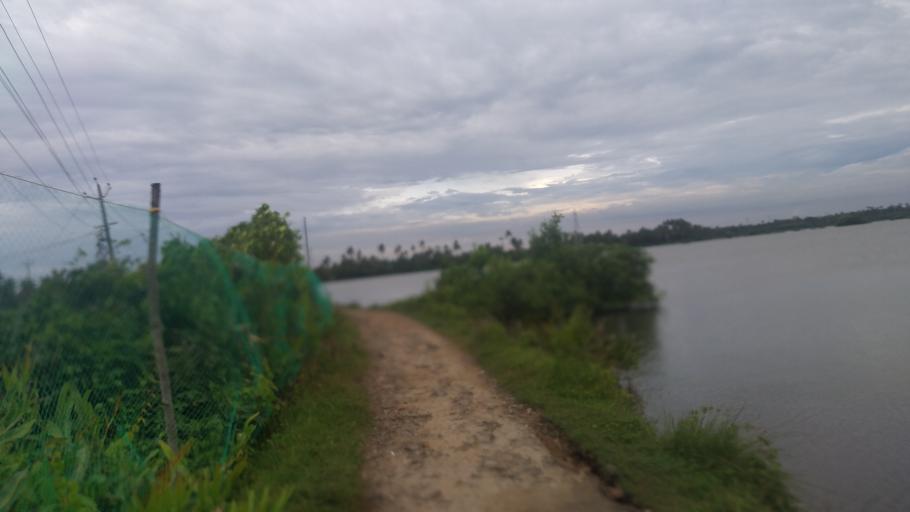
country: IN
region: Kerala
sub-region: Alappuzha
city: Arukutti
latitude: 9.8685
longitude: 76.2770
